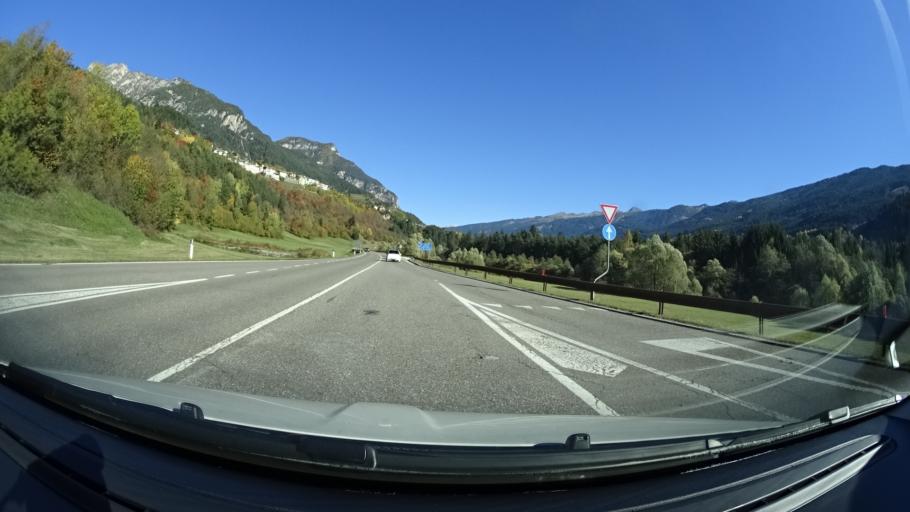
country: IT
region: Trentino-Alto Adige
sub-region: Provincia di Trento
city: Tesero
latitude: 46.2860
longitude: 11.4950
